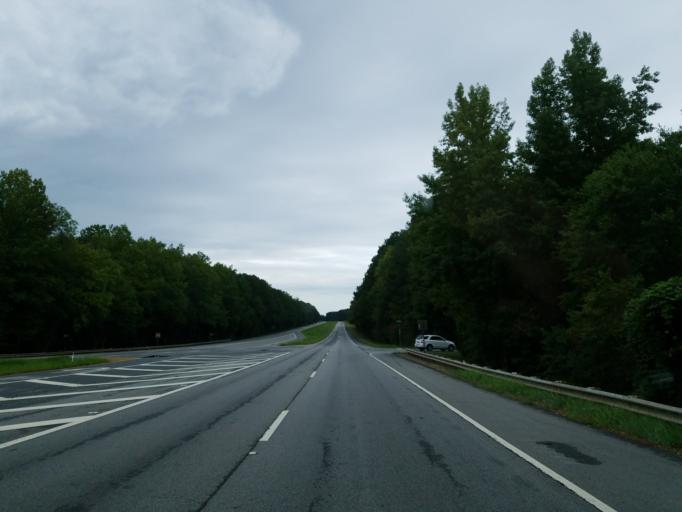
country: US
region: Georgia
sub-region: Lamar County
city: Barnesville
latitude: 33.1225
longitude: -84.2172
